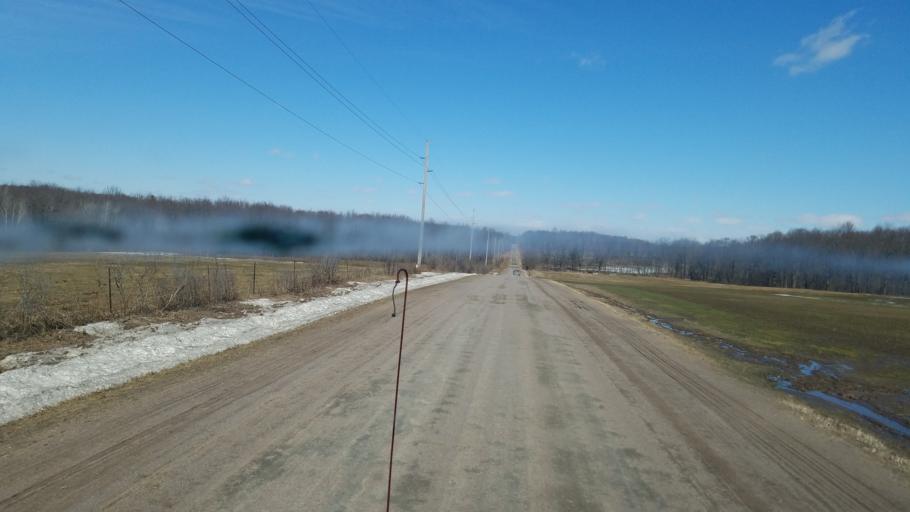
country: US
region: Wisconsin
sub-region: Clark County
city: Loyal
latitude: 44.5996
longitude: -90.3965
